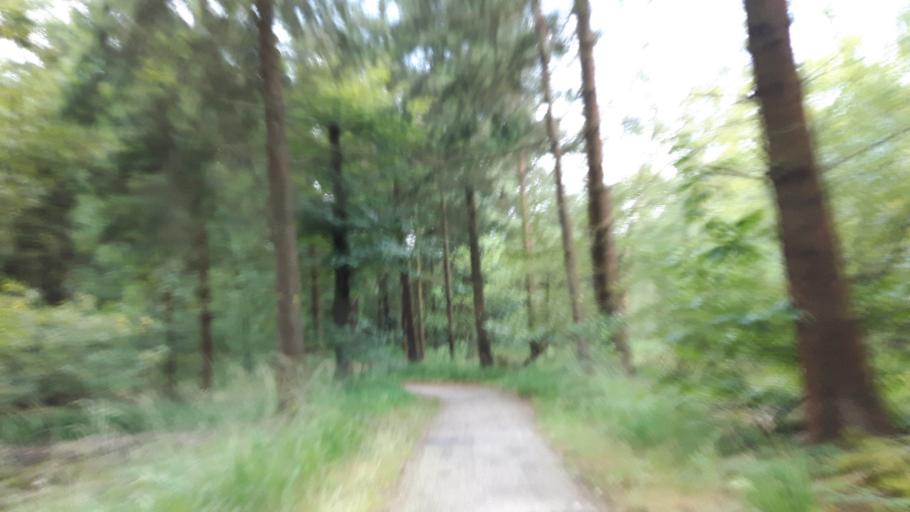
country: NL
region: Friesland
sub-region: Gemeente Smallingerland
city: Drachtstercompagnie
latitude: 53.0728
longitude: 6.2115
